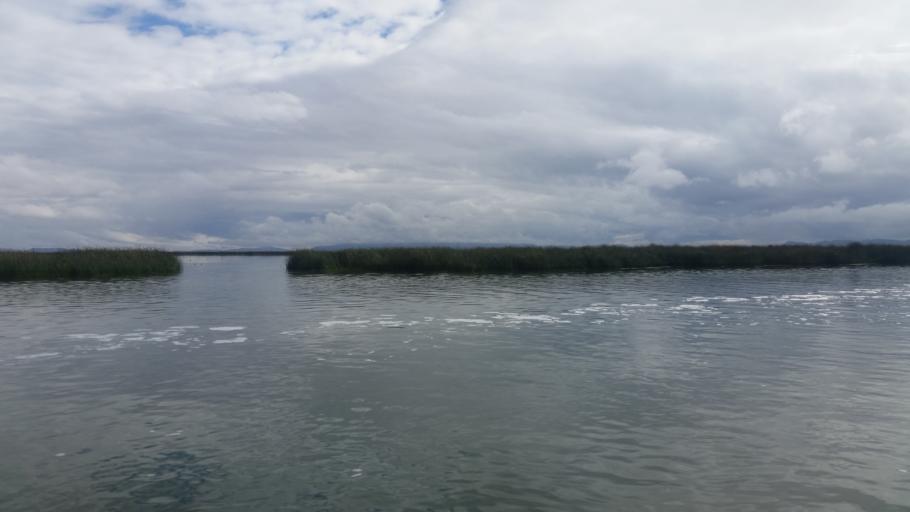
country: PE
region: Puno
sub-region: Provincia de Puno
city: Puno
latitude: -15.8451
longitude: -69.9780
